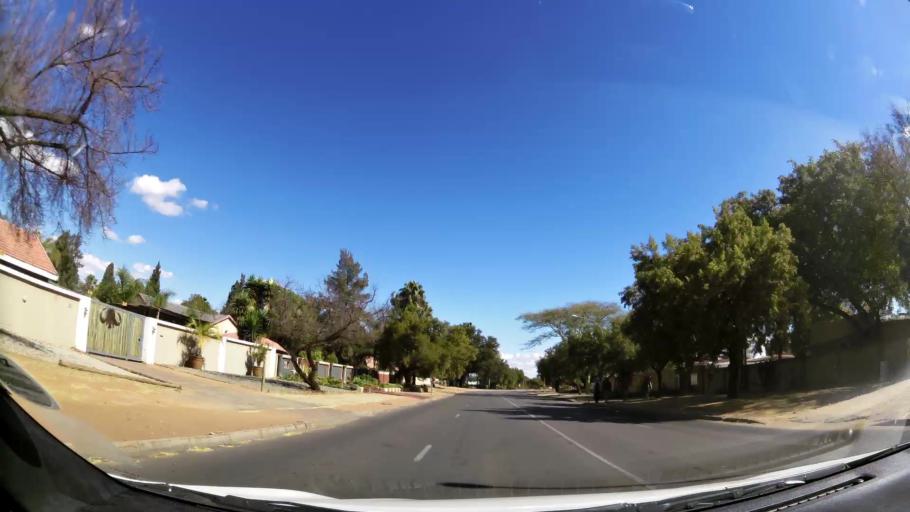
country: ZA
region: Limpopo
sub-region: Capricorn District Municipality
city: Polokwane
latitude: -23.9129
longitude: 29.4814
